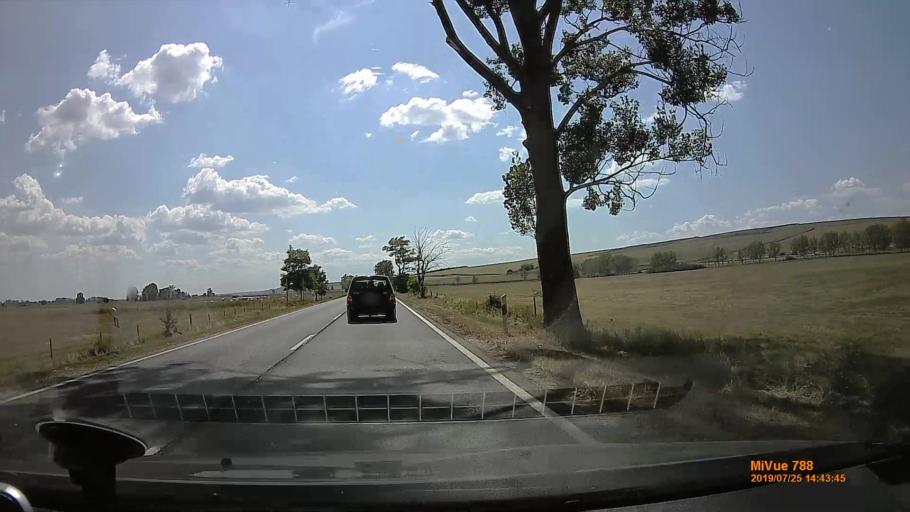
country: HU
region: Borsod-Abauj-Zemplen
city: Halmaj
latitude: 48.2713
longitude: 21.0077
